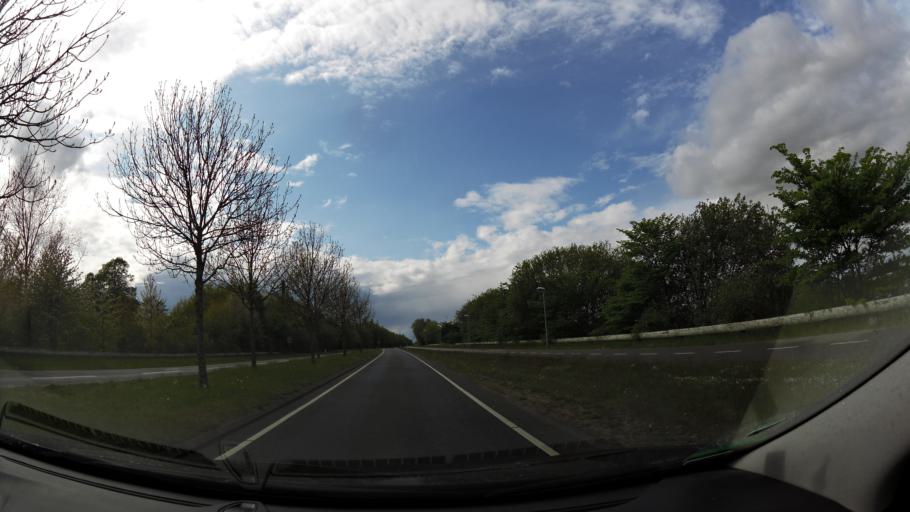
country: DK
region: South Denmark
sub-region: Nyborg Kommune
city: Nyborg
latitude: 55.3124
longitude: 10.7679
